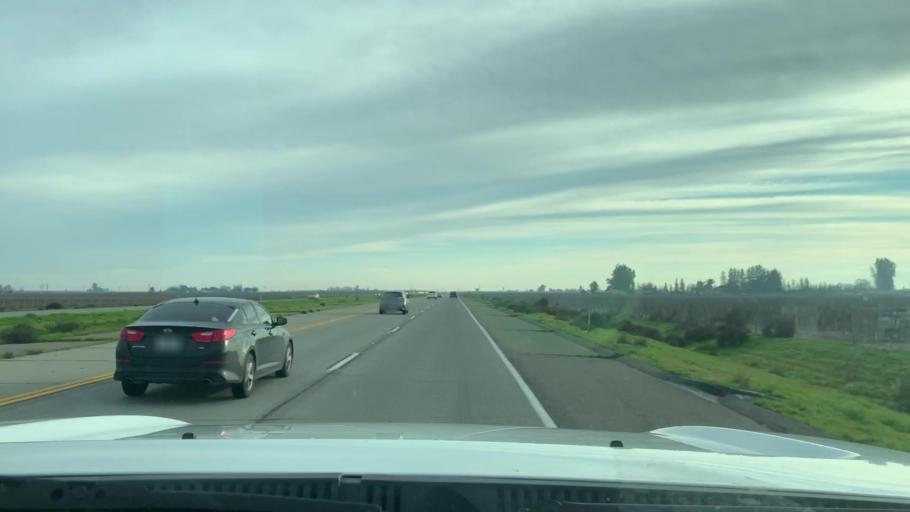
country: US
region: California
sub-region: Fresno County
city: Caruthers
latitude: 36.5603
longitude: -119.7863
